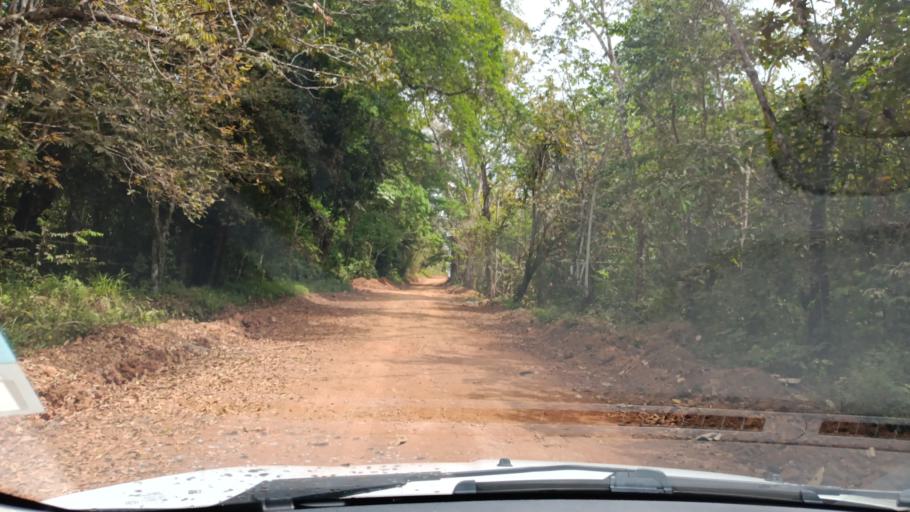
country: PA
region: Panama
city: La Cabima
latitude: 9.1306
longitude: -79.5020
